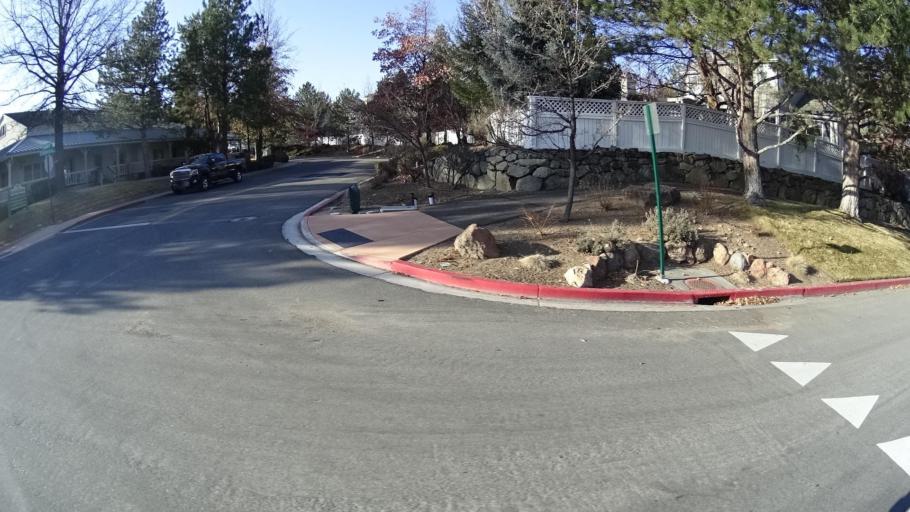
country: US
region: Nevada
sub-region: Washoe County
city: Reno
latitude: 39.5011
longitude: -119.8600
